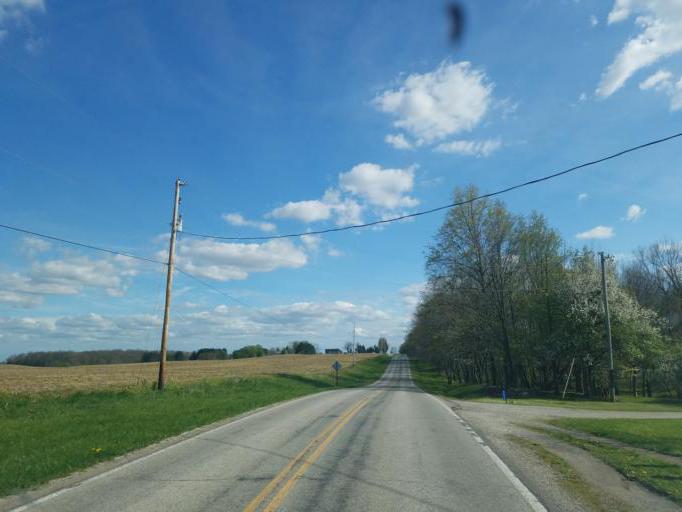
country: US
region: Ohio
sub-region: Huron County
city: Plymouth
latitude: 40.9751
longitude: -82.6569
